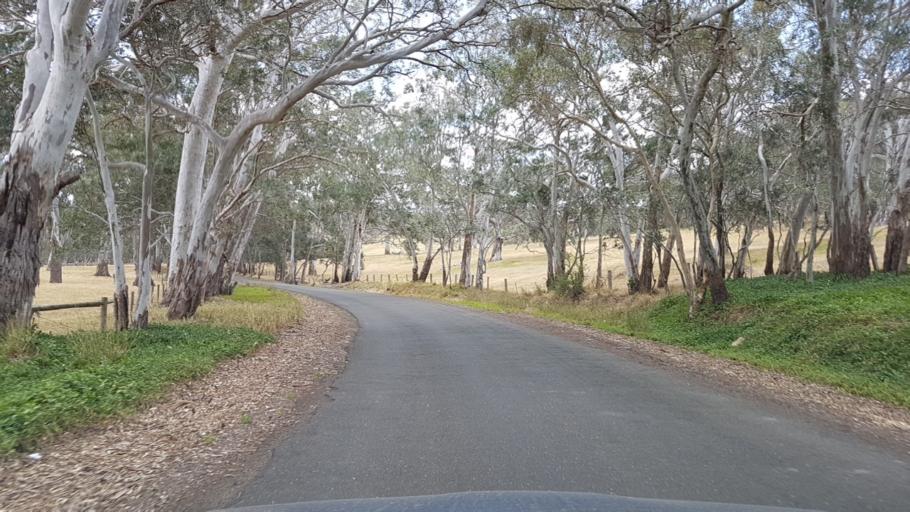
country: AU
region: South Australia
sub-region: Victor Harbor
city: Victor Harbor
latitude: -35.4785
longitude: 138.6077
